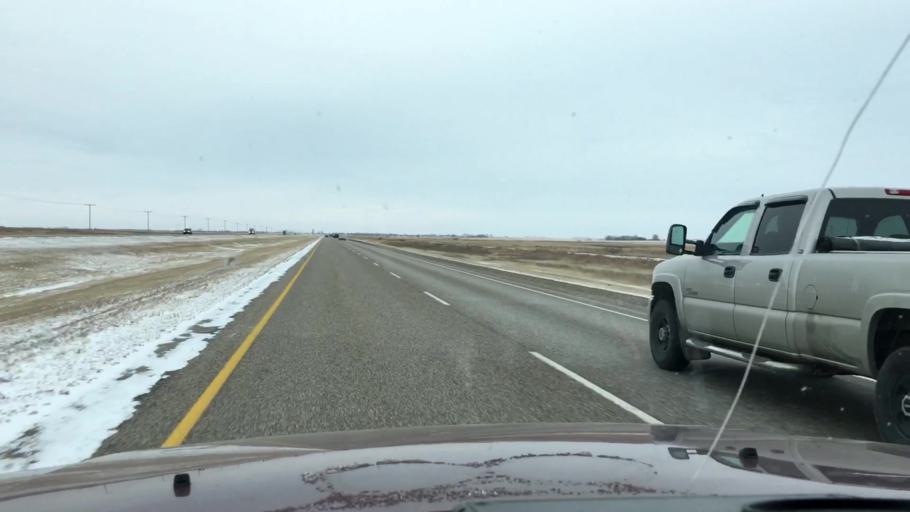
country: CA
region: Saskatchewan
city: Watrous
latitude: 51.0905
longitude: -105.8575
